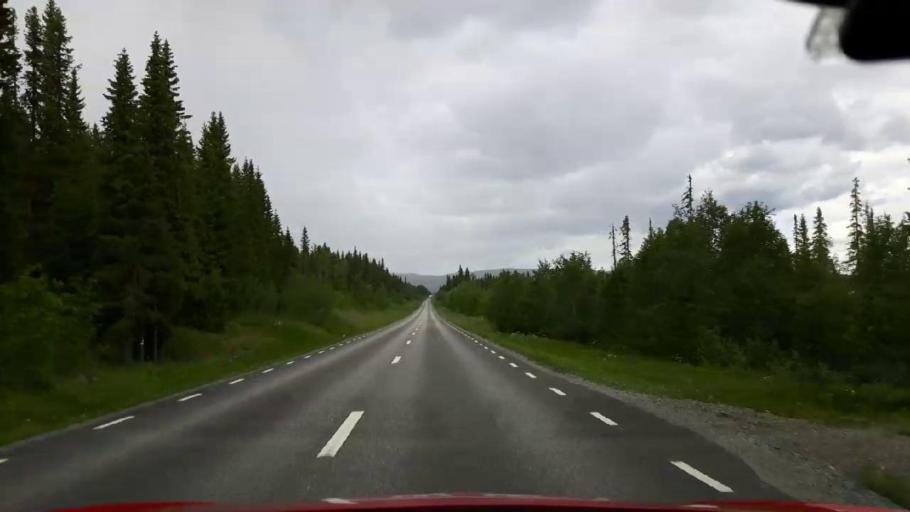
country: SE
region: Jaemtland
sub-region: Krokoms Kommun
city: Krokom
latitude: 63.7080
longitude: 14.3102
